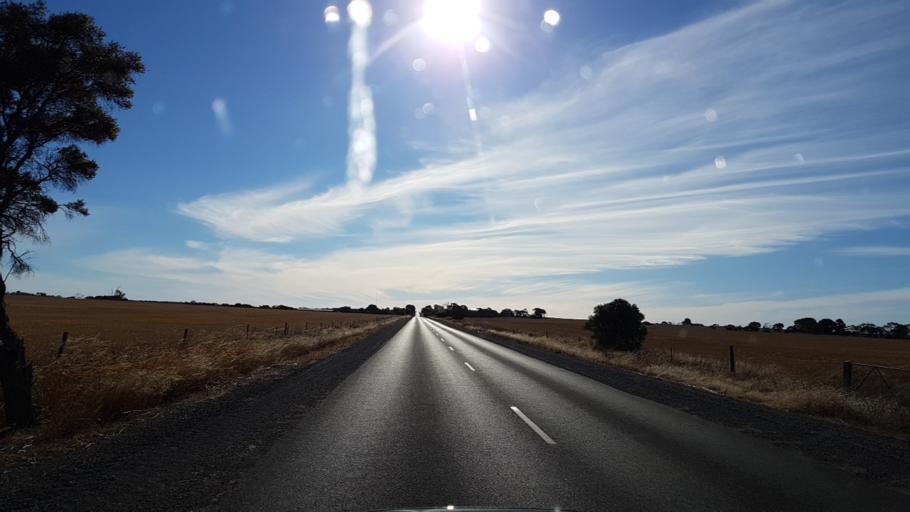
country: AU
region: South Australia
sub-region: Yorke Peninsula
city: Honiton
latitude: -34.9850
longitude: 137.3055
